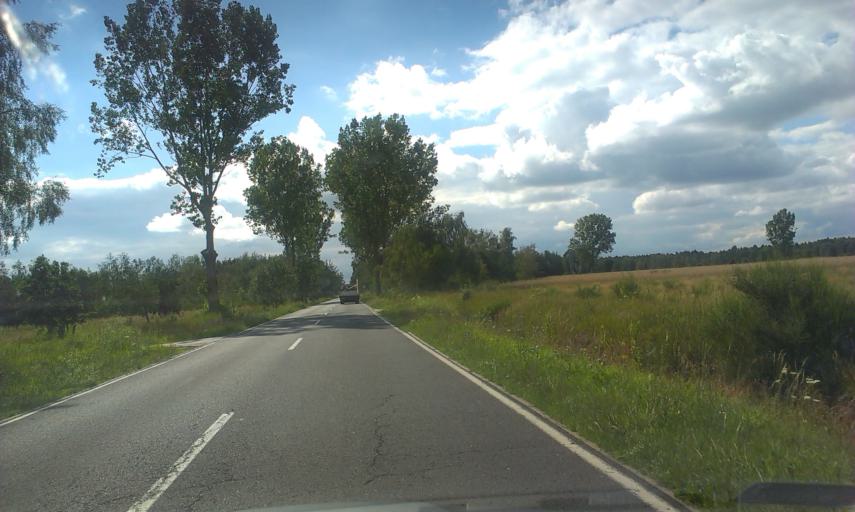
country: PL
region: Lodz Voivodeship
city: Zabia Wola
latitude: 51.9667
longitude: 20.6578
